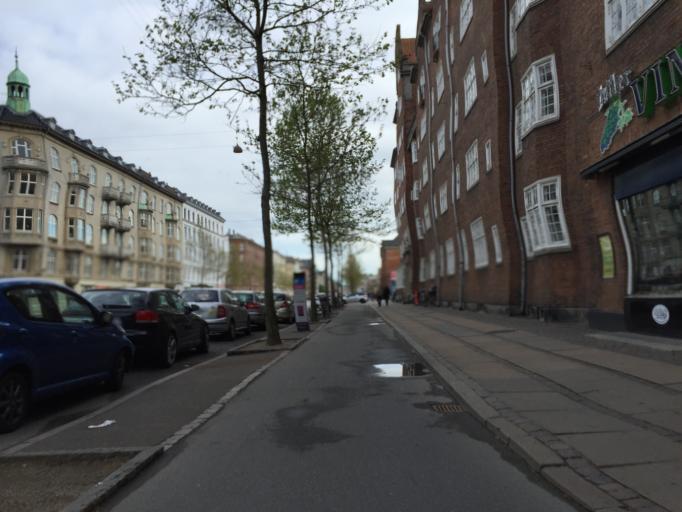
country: DK
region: Capital Region
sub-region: Kobenhavn
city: Copenhagen
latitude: 55.7073
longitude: 12.5772
